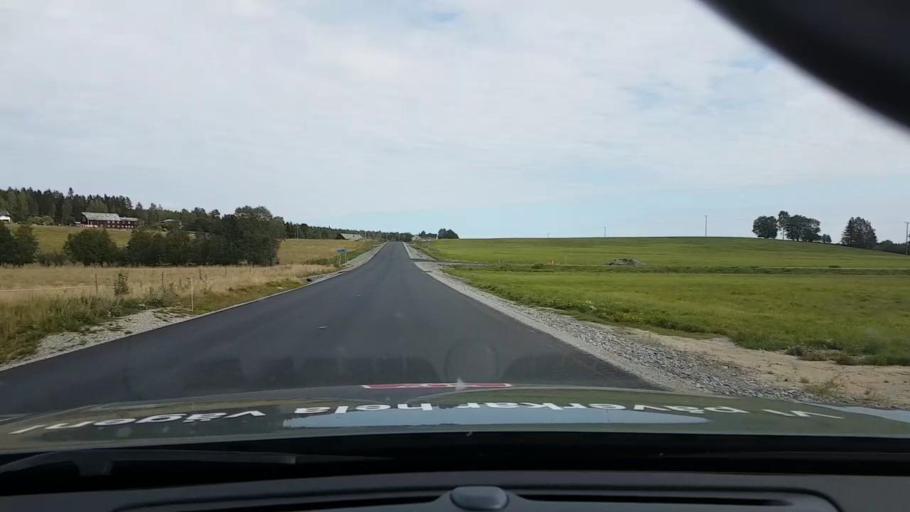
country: SE
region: Vaesternorrland
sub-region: OErnskoeldsviks Kommun
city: Bjasta
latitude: 63.2901
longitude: 18.4577
